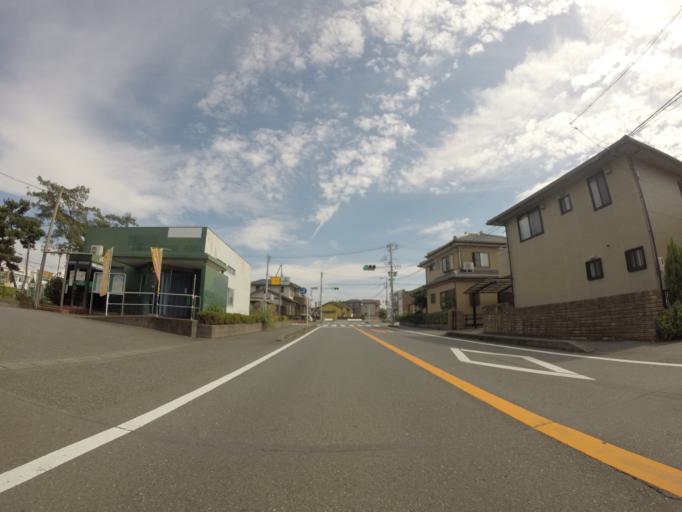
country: JP
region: Shizuoka
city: Fuji
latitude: 35.1231
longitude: 138.6183
